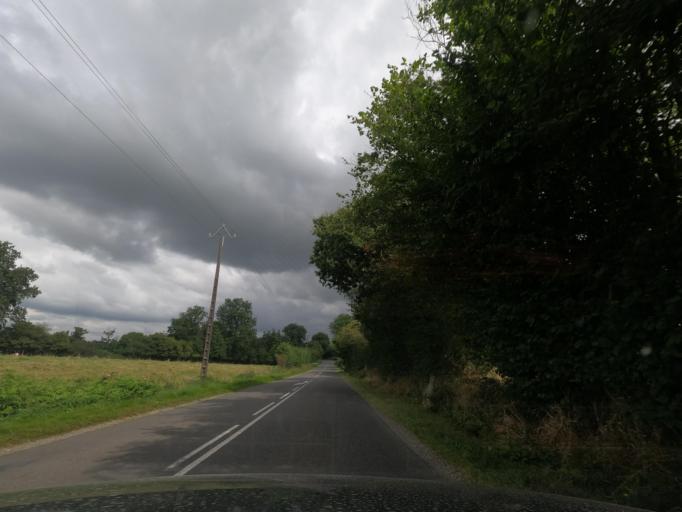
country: FR
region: Lower Normandy
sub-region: Departement de l'Orne
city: Briouze
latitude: 48.6924
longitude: -0.4158
